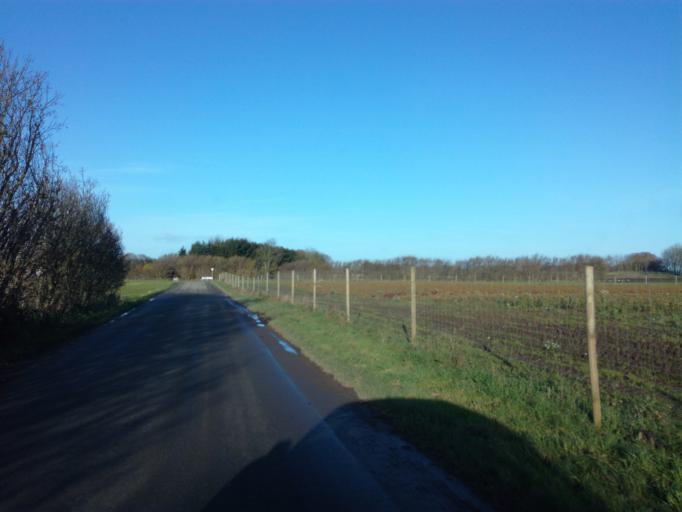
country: DK
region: South Denmark
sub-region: Vejle Kommune
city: Borkop
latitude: 55.6282
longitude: 9.6776
